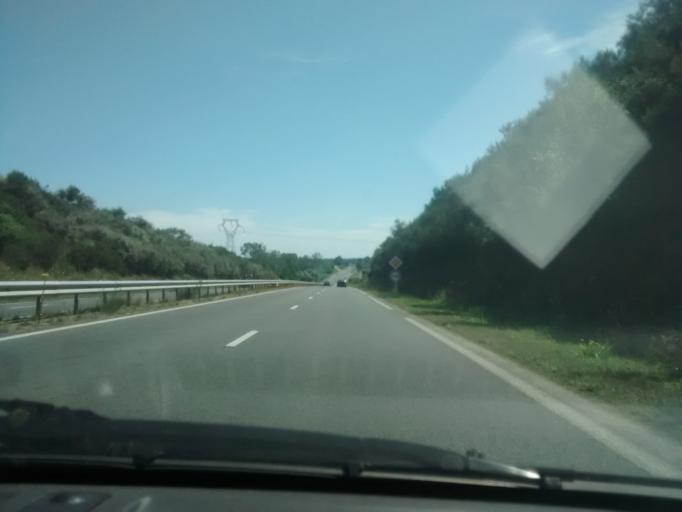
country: FR
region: Brittany
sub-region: Departement des Cotes-d'Armor
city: Rospez
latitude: 48.7000
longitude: -3.3760
